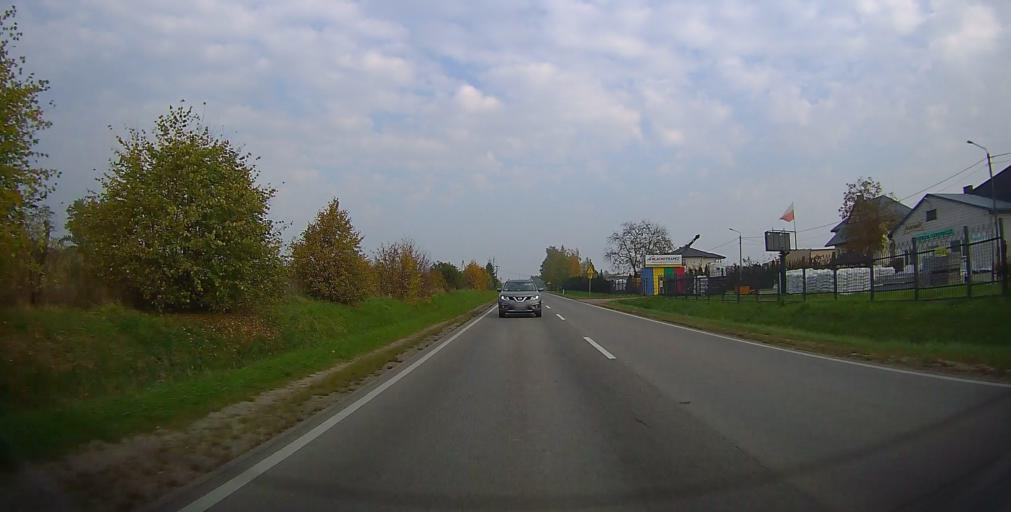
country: PL
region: Masovian Voivodeship
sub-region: Powiat grojecki
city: Belsk Duzy
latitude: 51.7845
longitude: 20.7773
